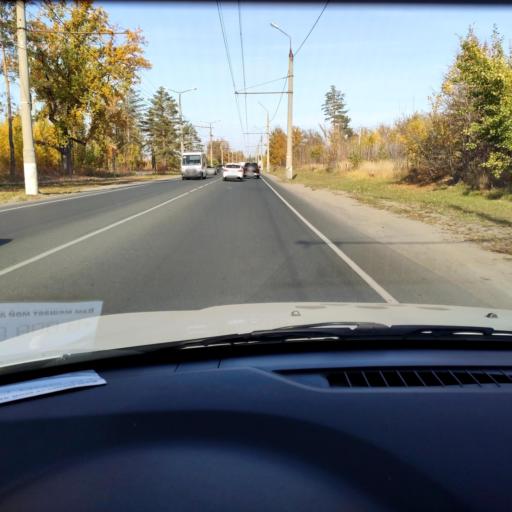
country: RU
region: Samara
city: Tol'yatti
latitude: 53.4843
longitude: 49.3802
